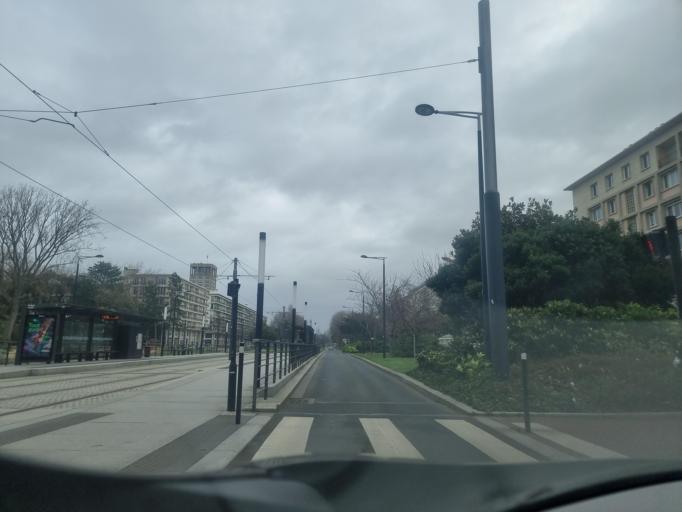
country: FR
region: Haute-Normandie
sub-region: Departement de la Seine-Maritime
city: Le Havre
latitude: 49.4935
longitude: 0.0998
